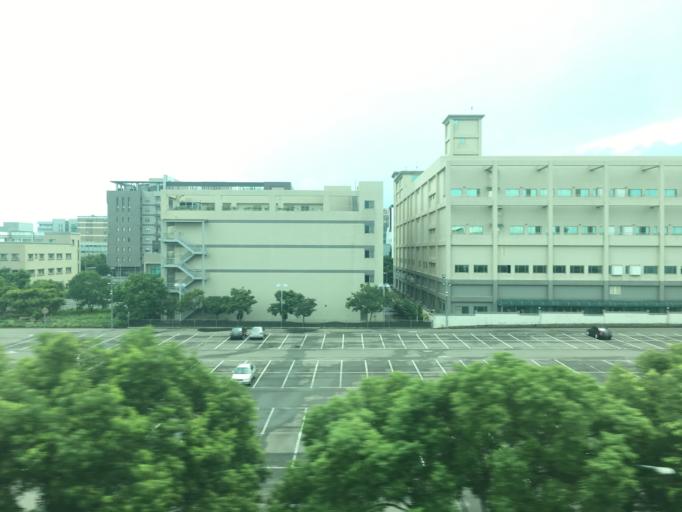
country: TW
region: Taiwan
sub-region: Taoyuan
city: Taoyuan
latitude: 25.0527
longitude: 121.3785
